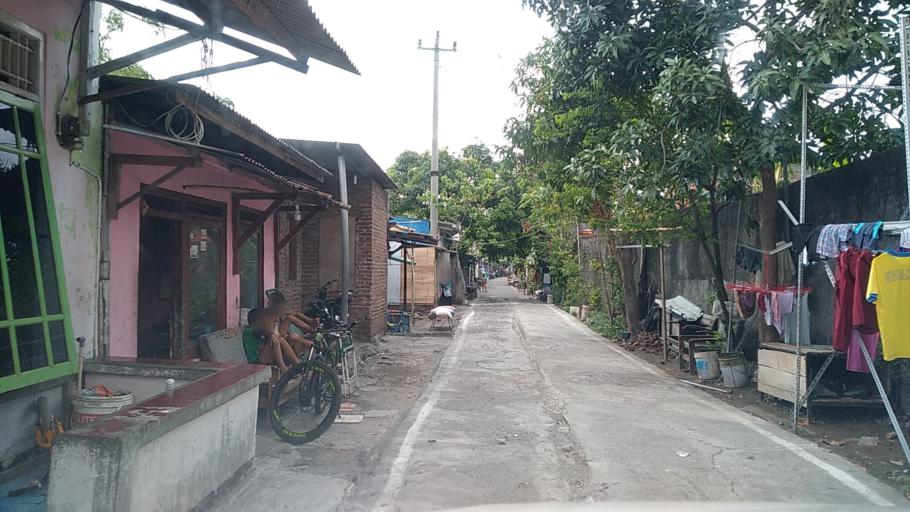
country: ID
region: Central Java
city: Semarang
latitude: -7.0012
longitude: 110.4437
